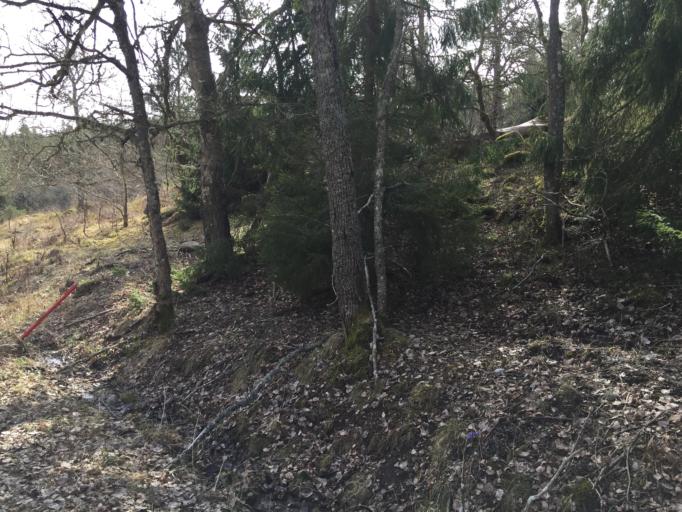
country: SE
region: Stockholm
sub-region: Salems Kommun
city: Ronninge
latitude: 59.2513
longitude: 17.6912
